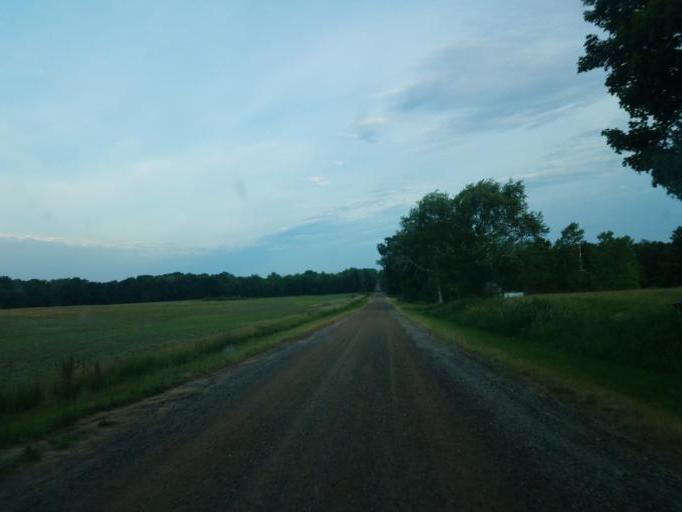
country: US
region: Michigan
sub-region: Eaton County
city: Charlotte
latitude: 42.5972
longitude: -84.8982
